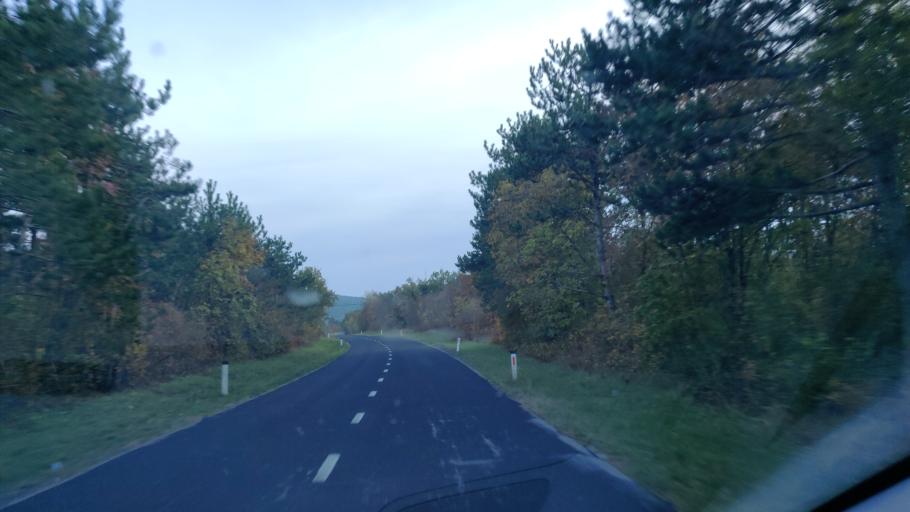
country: SI
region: Sezana
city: Sezana
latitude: 45.7471
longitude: 13.9263
